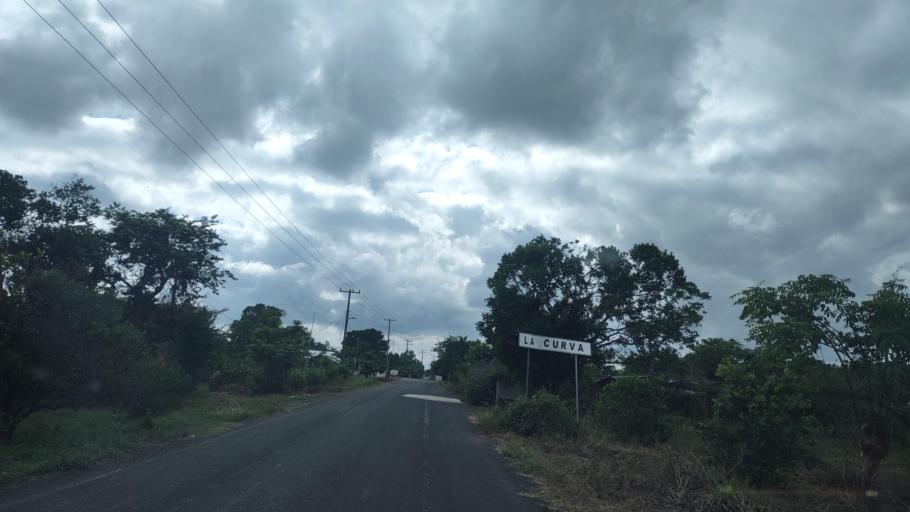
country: MX
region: Veracruz
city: Gutierrez Zamora
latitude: 20.2869
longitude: -97.1303
